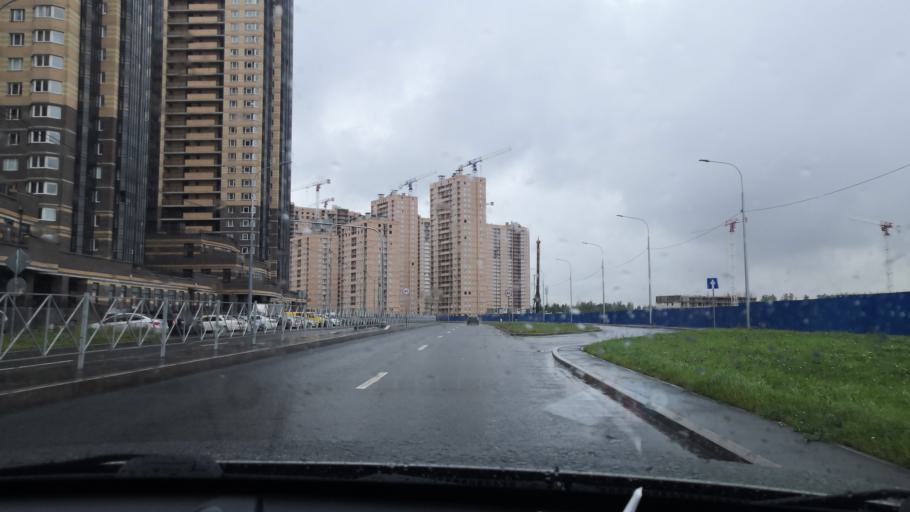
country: RU
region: Leningrad
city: Parnas
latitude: 60.0834
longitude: 30.3534
